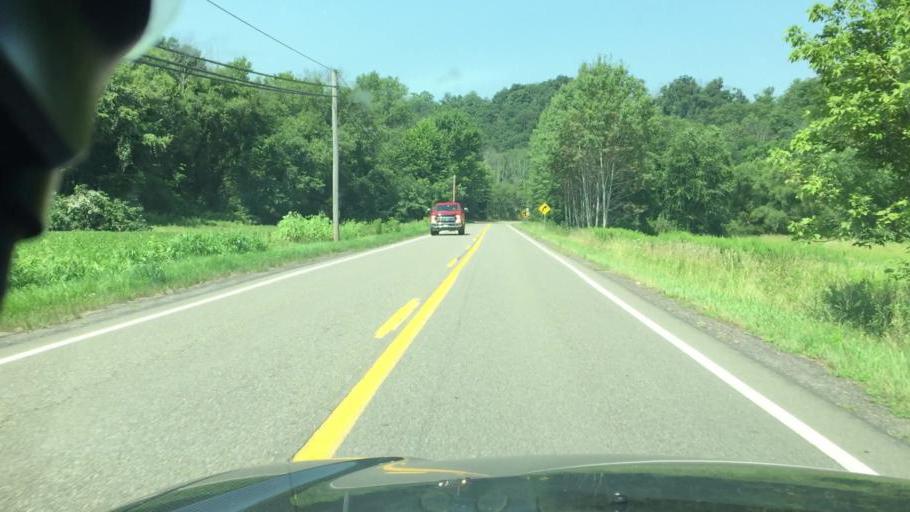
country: US
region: Pennsylvania
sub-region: Columbia County
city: Almedia
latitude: 40.9808
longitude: -76.3845
